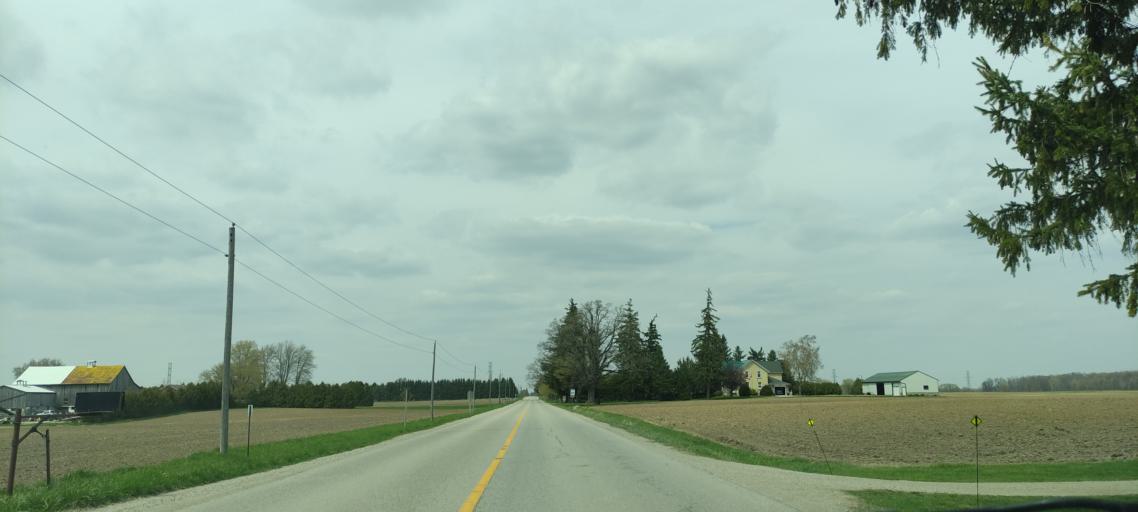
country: CA
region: Ontario
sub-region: Oxford County
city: Woodstock
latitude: 43.2825
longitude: -80.7649
